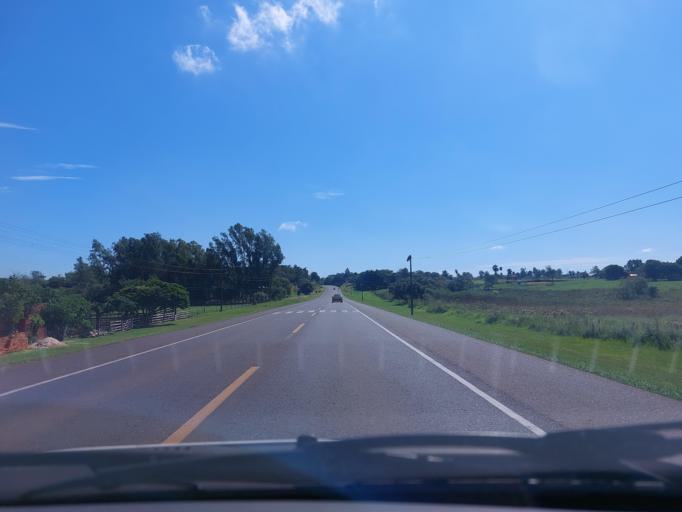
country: PY
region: San Pedro
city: Guayaybi
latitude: -24.6454
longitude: -56.4692
